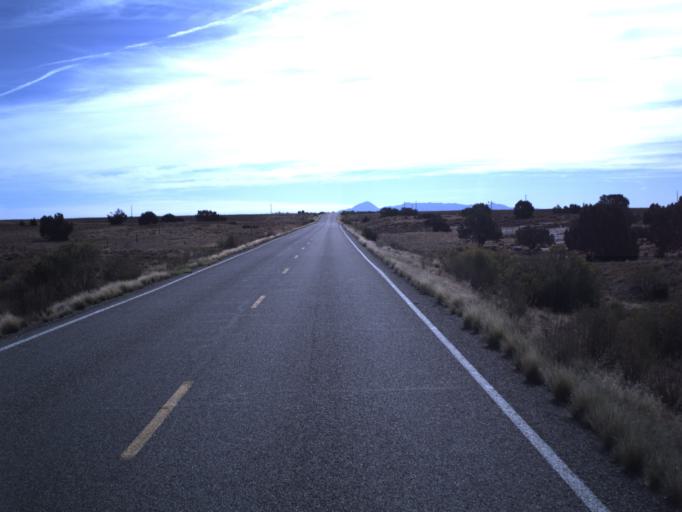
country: US
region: Utah
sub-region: San Juan County
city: Blanding
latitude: 37.4348
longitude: -109.3774
